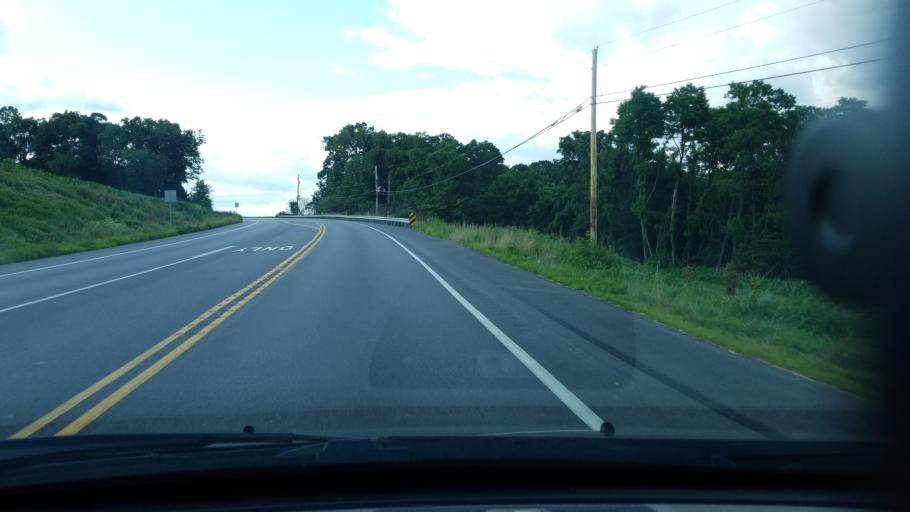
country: US
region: Pennsylvania
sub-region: Northumberland County
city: Elysburg
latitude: 40.9028
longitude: -76.5791
